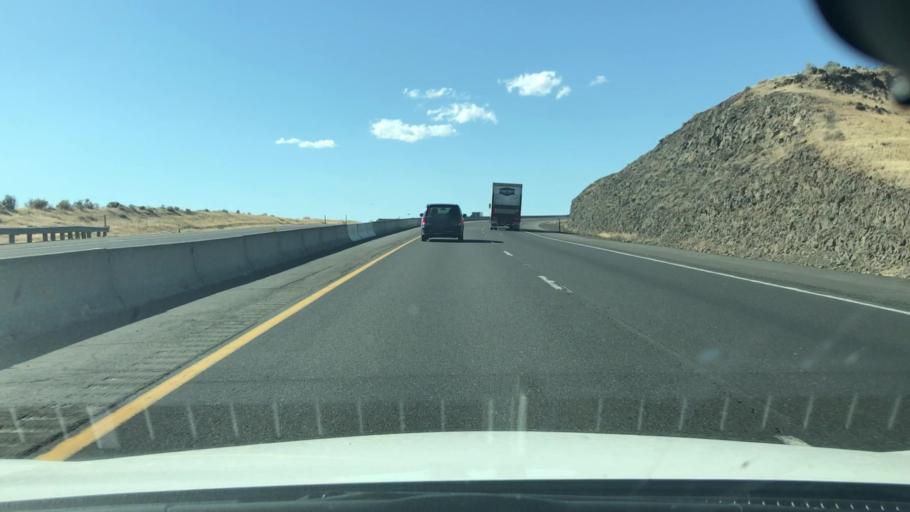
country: US
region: Washington
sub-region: Grant County
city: Mattawa
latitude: 46.9620
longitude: -119.9654
